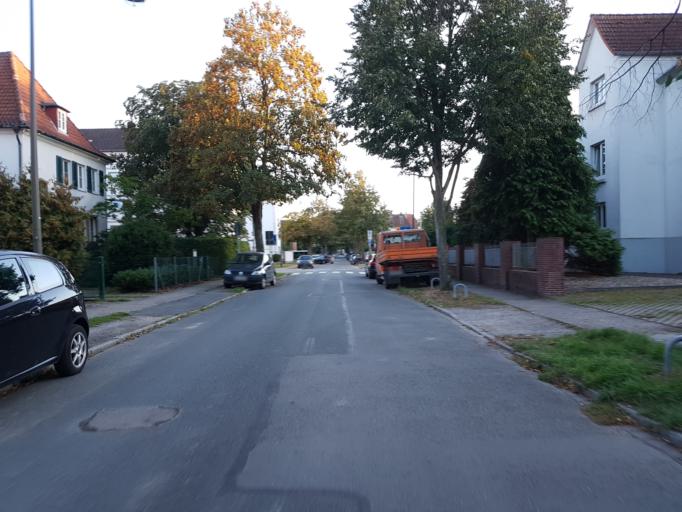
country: DE
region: Lower Saxony
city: Langenhagen
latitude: 52.4429
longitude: 9.7351
